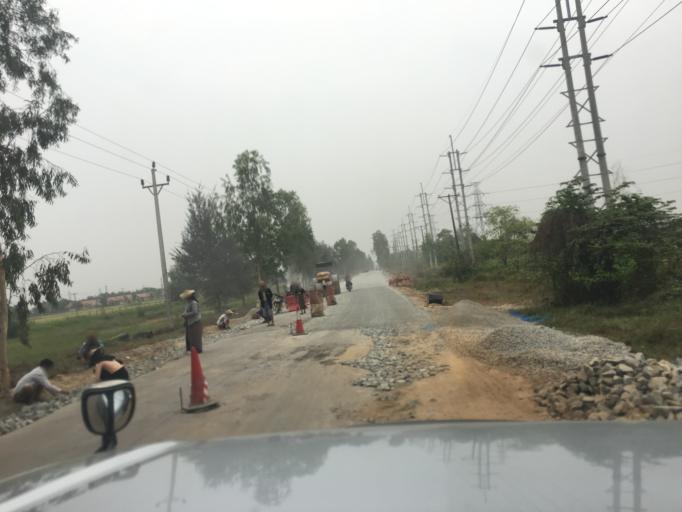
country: MM
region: Yangon
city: Syriam
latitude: 16.9531
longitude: 96.2719
